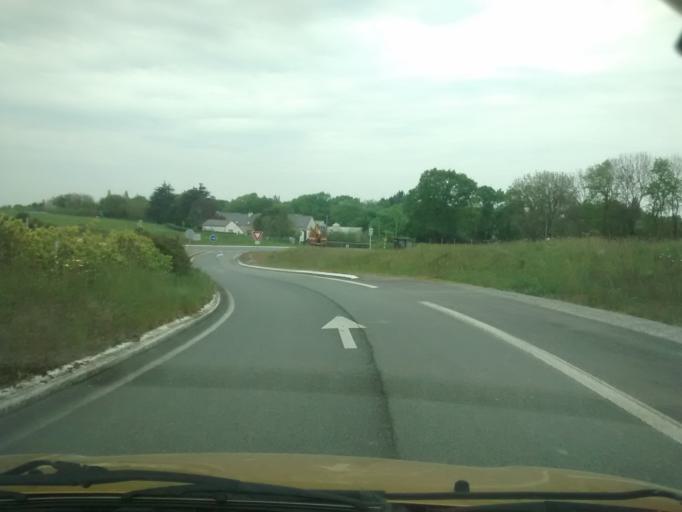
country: FR
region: Brittany
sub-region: Departement du Morbihan
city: Ambon
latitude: 47.5894
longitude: -2.5487
